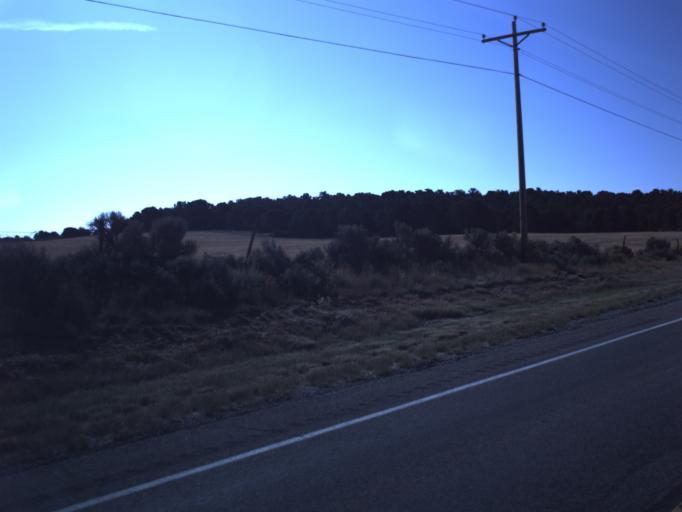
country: US
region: Utah
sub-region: San Juan County
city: Monticello
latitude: 37.9207
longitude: -109.3461
